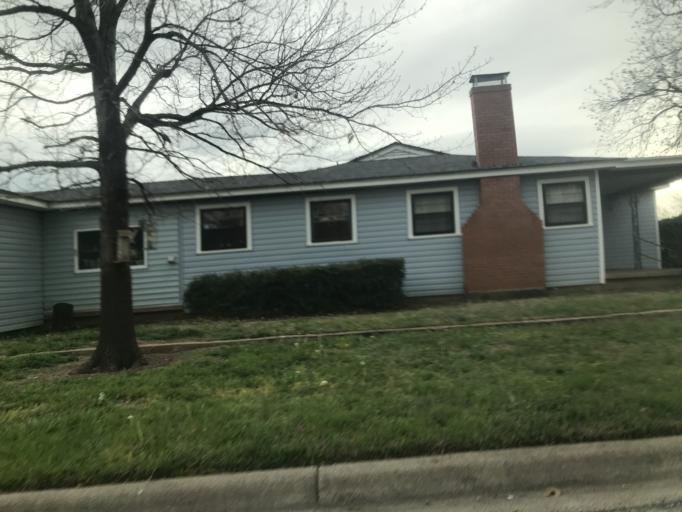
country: US
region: Texas
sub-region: Taylor County
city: Abilene
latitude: 32.4671
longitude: -99.7428
